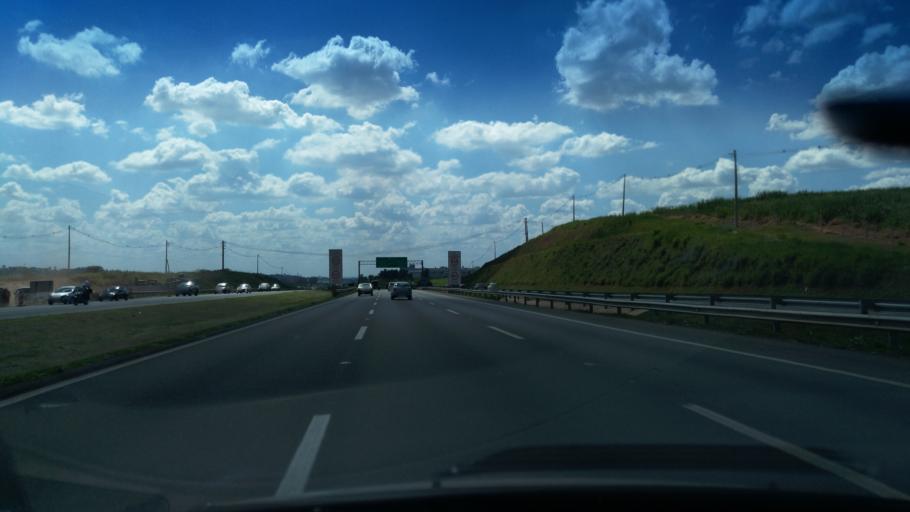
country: BR
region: Sao Paulo
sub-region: Campinas
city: Campinas
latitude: -22.8592
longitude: -47.0230
